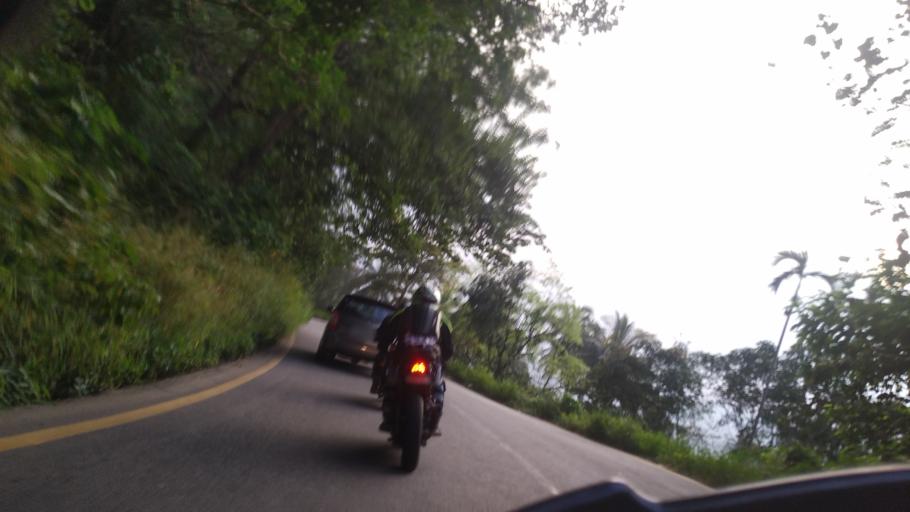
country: IN
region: Kerala
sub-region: Wayanad
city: Kalpetta
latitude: 11.4982
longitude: 76.0219
